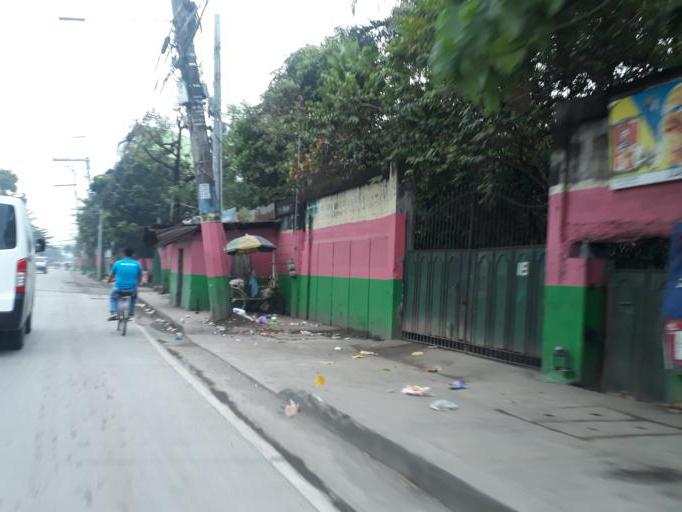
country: PH
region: Calabarzon
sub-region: Province of Rizal
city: Valenzuela
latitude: 14.6916
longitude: 120.9559
